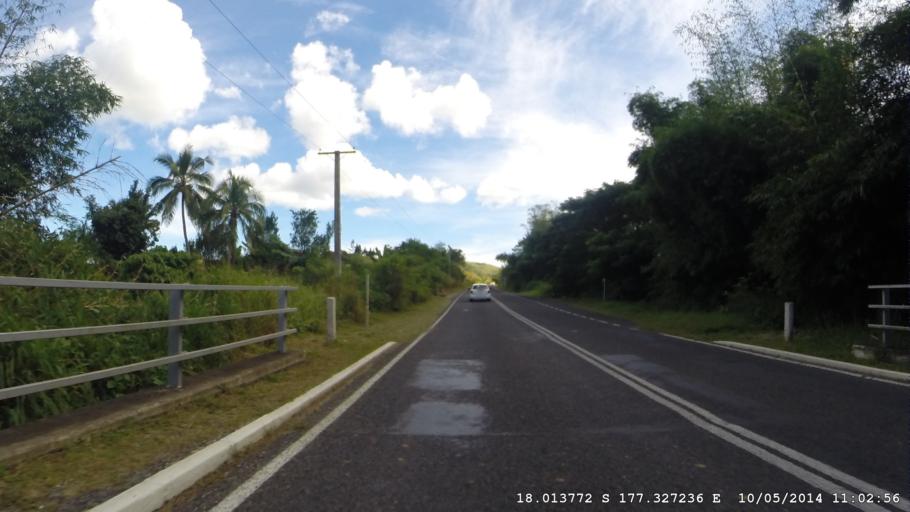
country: FJ
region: Western
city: Nadi
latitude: -18.0138
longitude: 177.3272
